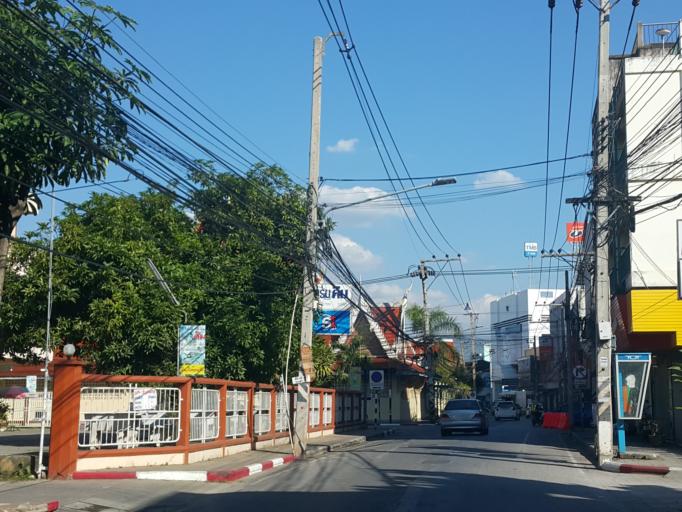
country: TH
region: Lampang
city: Lampang
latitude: 18.2886
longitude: 99.4953
